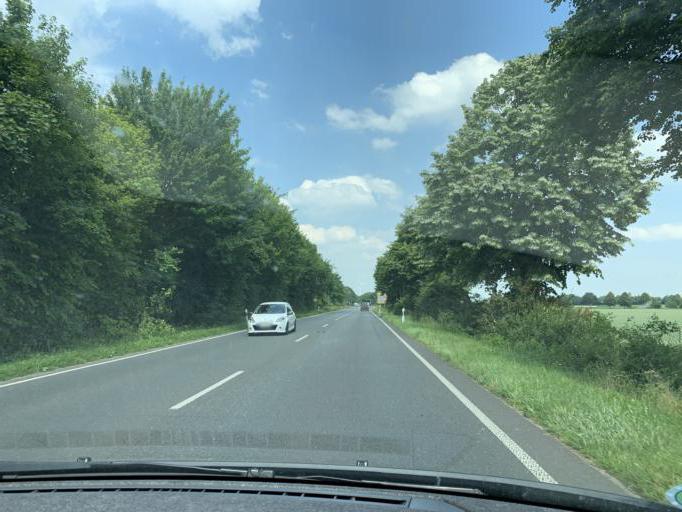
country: DE
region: North Rhine-Westphalia
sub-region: Regierungsbezirk Koln
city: Eschweiler
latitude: 50.8335
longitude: 6.2458
